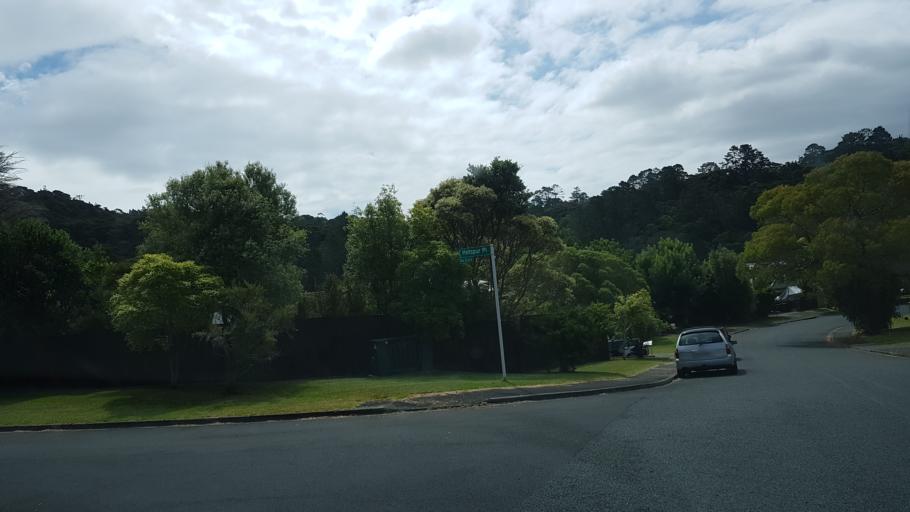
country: NZ
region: Auckland
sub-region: Auckland
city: North Shore
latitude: -36.7755
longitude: 174.7013
